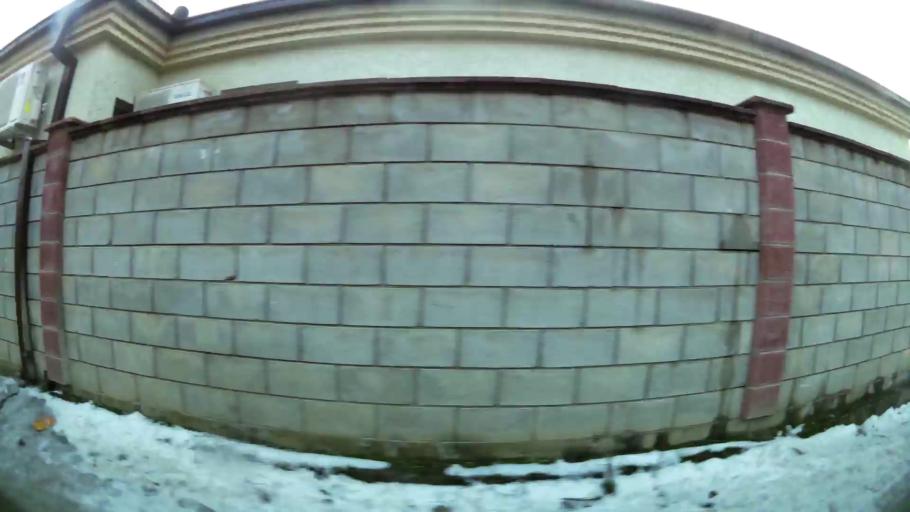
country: MK
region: Aracinovo
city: Arachinovo
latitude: 42.0221
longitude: 21.5604
